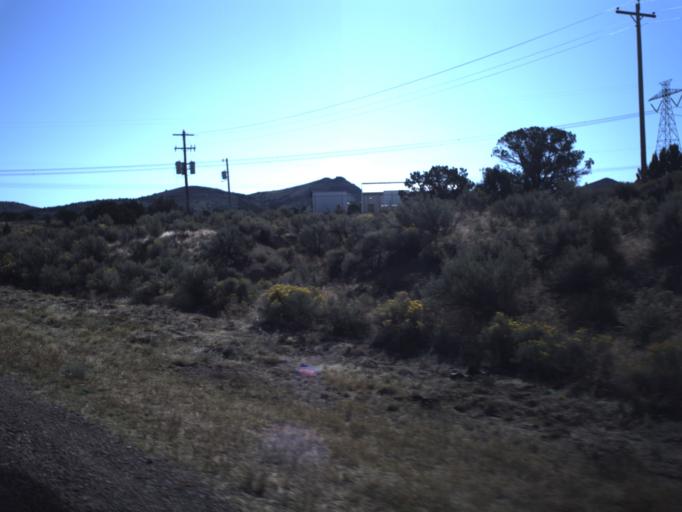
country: US
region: Utah
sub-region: Washington County
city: Enterprise
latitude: 37.6737
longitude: -113.5329
